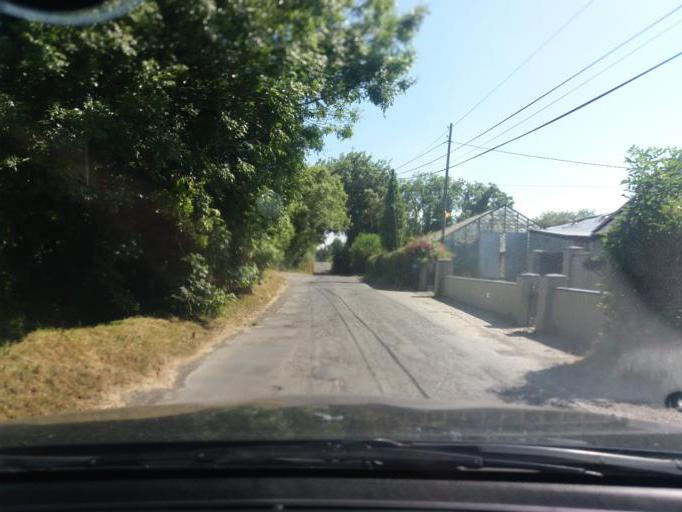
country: IE
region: Leinster
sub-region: Fingal County
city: Swords
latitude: 53.4880
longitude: -6.2852
